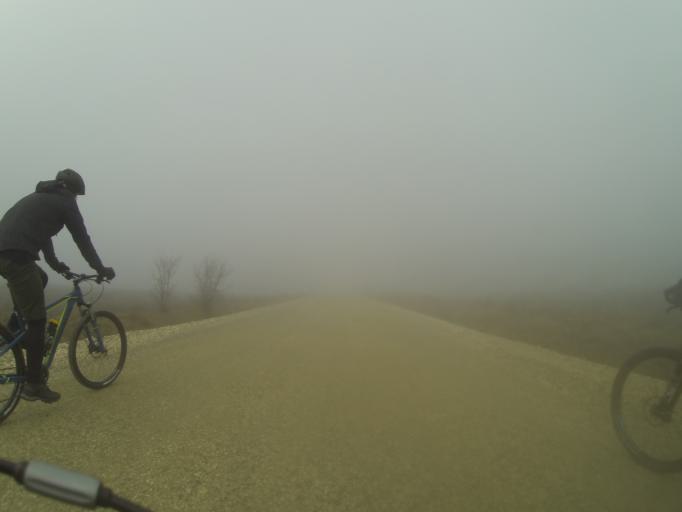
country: RO
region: Mehedinti
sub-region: Comuna Baclesu
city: Baclesu
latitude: 44.4471
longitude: 23.1269
